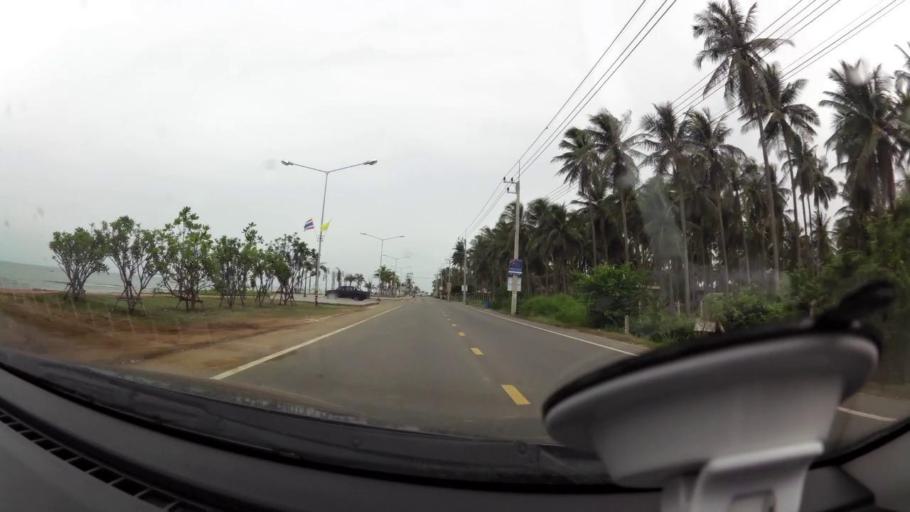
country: TH
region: Prachuap Khiri Khan
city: Pran Buri
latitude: 12.3893
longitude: 99.9977
